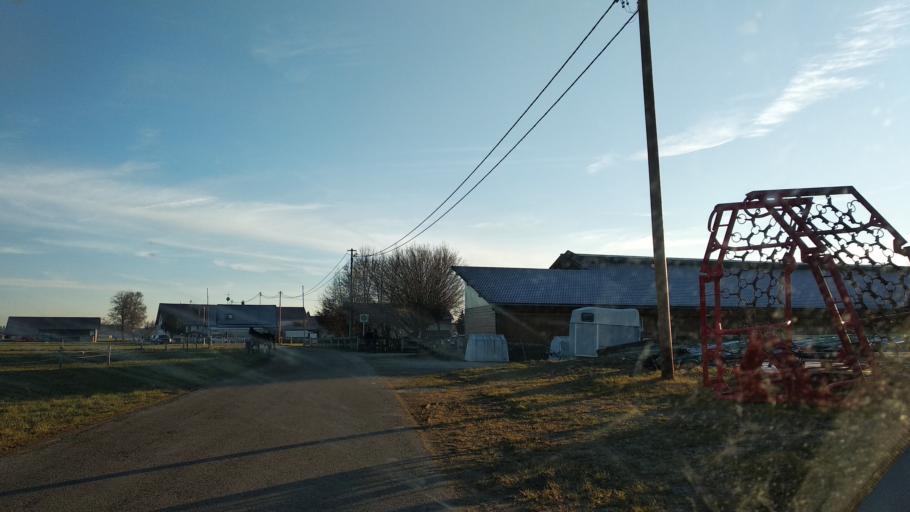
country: DE
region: Bavaria
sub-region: Swabia
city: Lautrach
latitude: 47.9153
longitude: 10.1300
